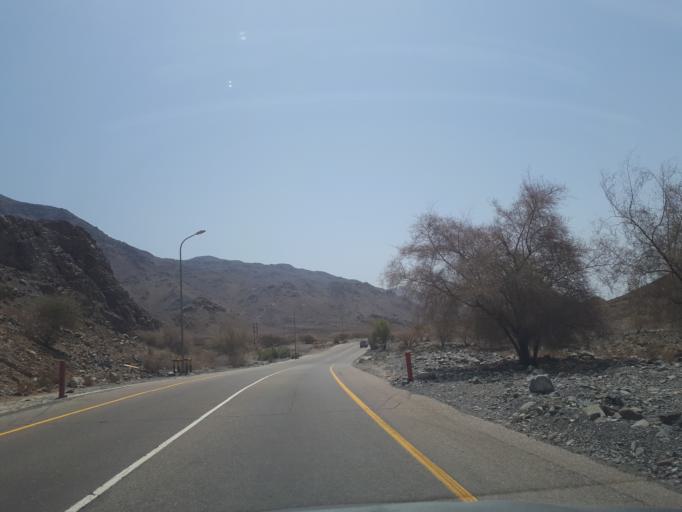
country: OM
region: Muhafazat ad Dakhiliyah
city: Sufalat Sama'il
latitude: 23.1713
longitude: 58.0975
